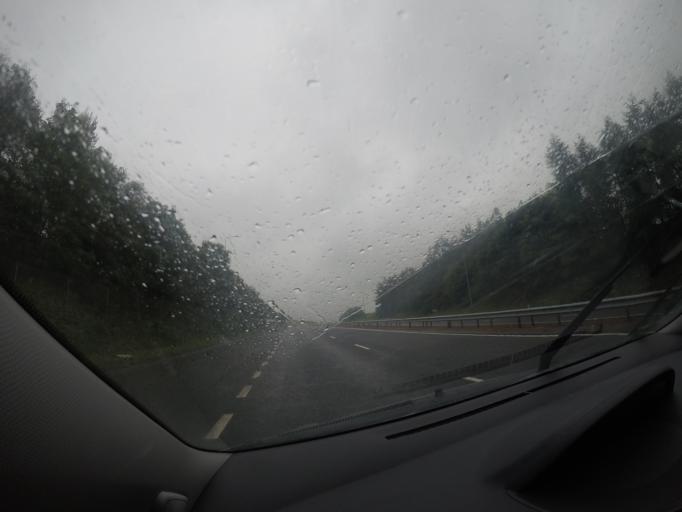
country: GB
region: Scotland
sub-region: Angus
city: Forfar
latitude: 56.5787
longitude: -2.9131
